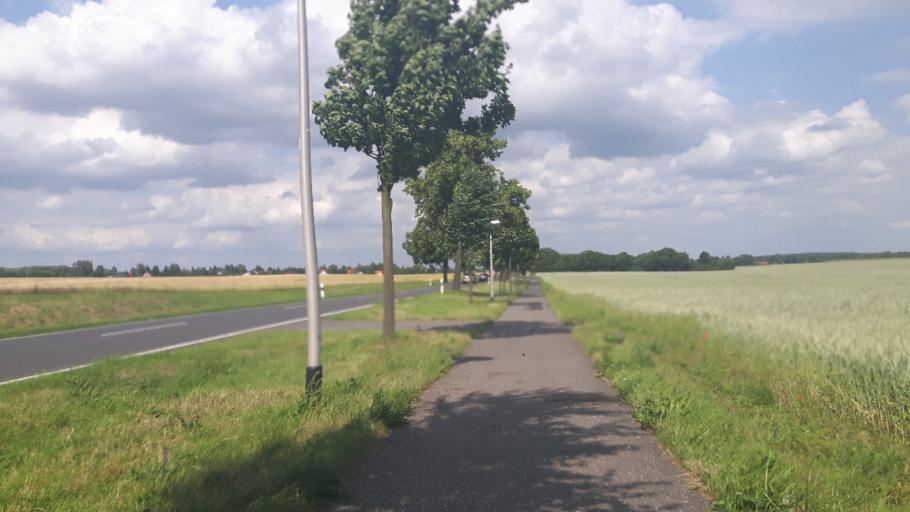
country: DE
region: Berlin
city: Buch
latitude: 52.6318
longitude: 13.5491
